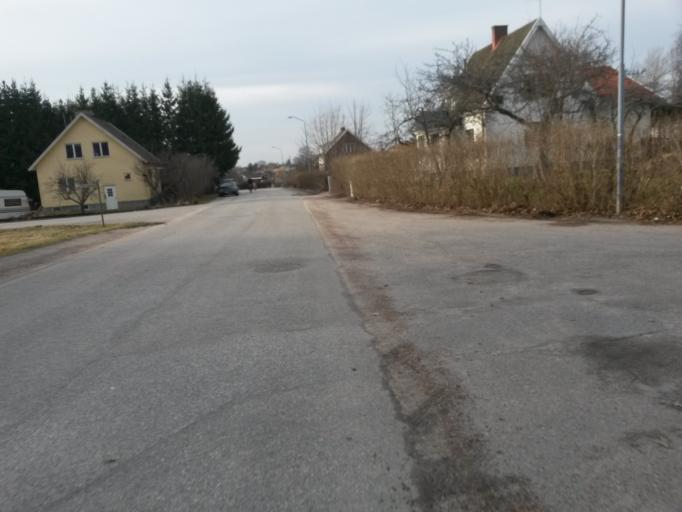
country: SE
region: Vaestra Goetaland
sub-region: Herrljunga Kommun
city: Herrljunga
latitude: 58.0719
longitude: 13.0306
